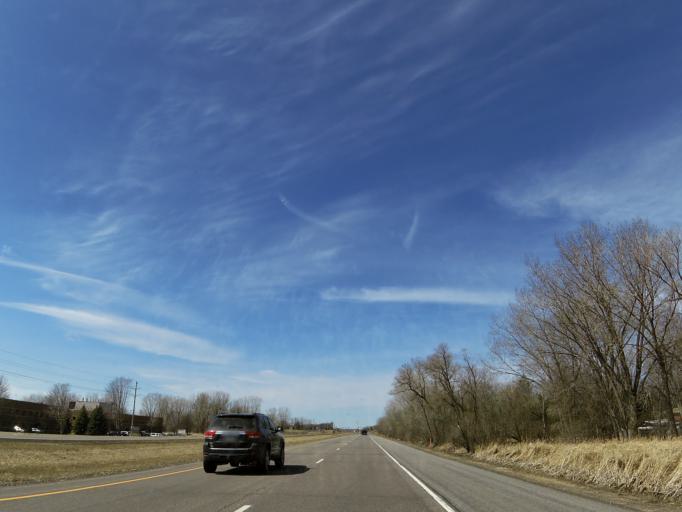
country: US
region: Minnesota
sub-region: Ramsey County
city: North Saint Paul
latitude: 44.9978
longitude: -92.9659
